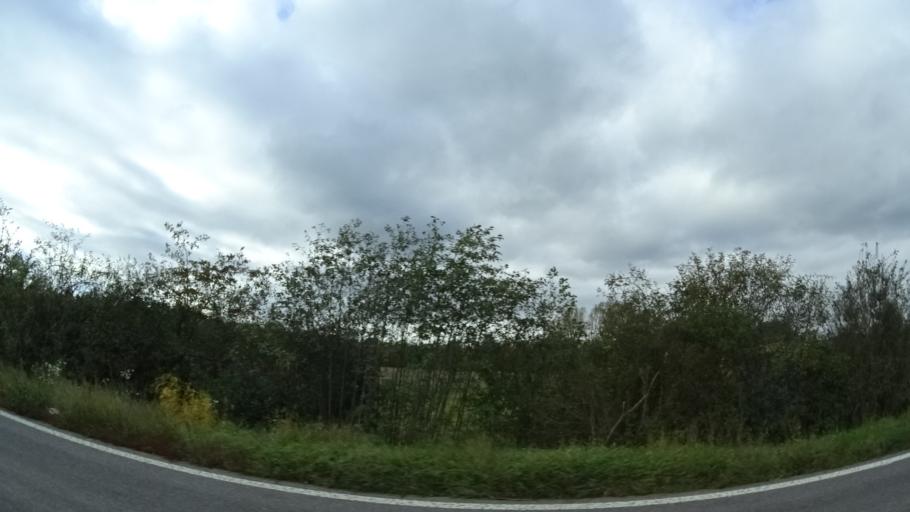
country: DE
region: Baden-Wuerttemberg
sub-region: Karlsruhe Region
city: Weingarten
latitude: 49.0807
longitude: 8.5065
